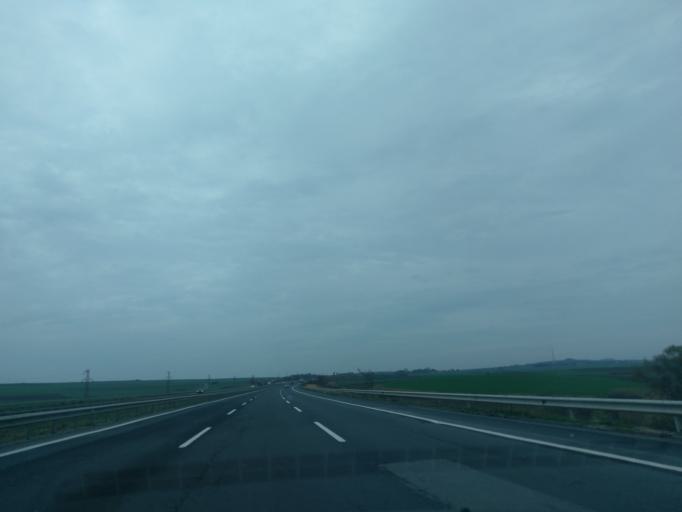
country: TR
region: Istanbul
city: Canta
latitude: 41.1271
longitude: 28.1633
